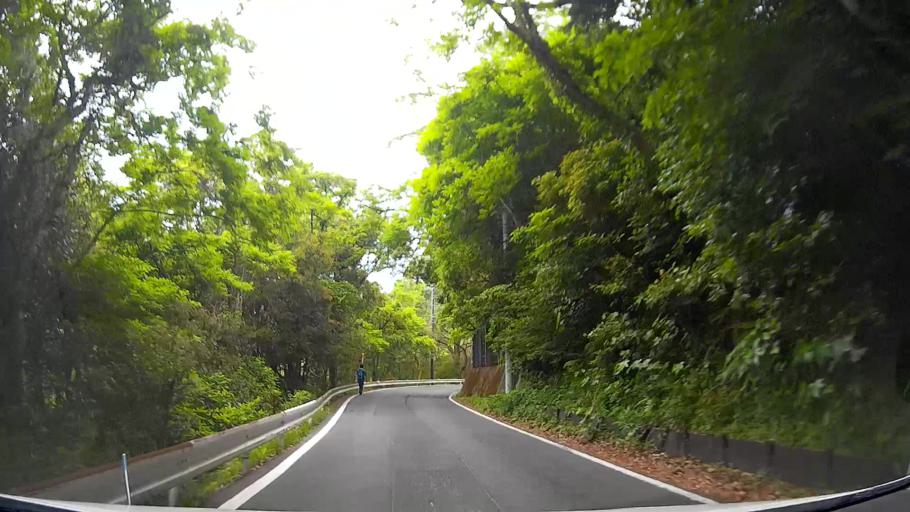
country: JP
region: Shizuoka
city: Ito
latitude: 34.9355
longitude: 139.1394
